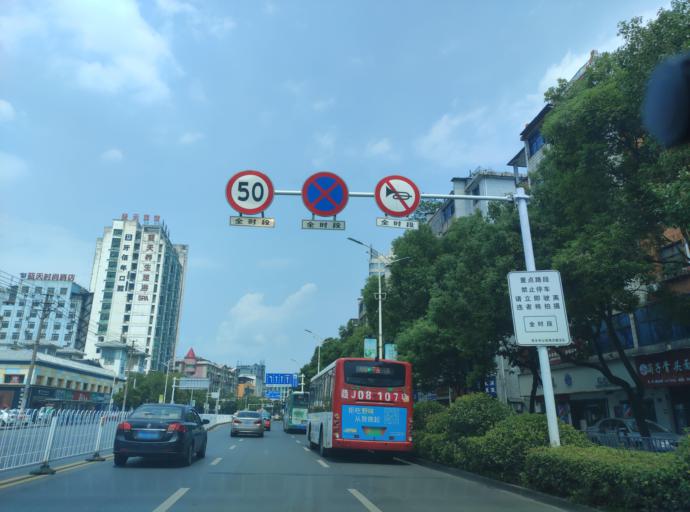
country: CN
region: Jiangxi Sheng
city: Pingxiang
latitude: 27.6414
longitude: 113.8618
